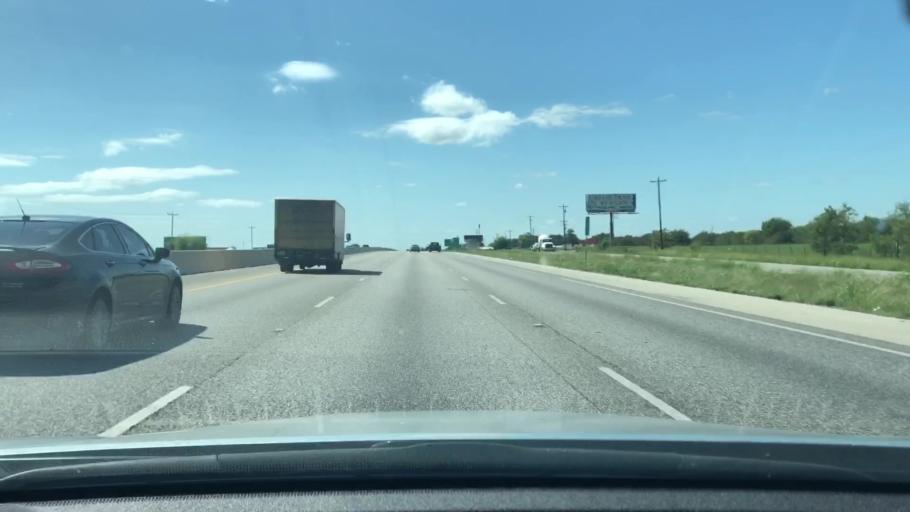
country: US
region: Texas
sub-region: Guadalupe County
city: Redwood
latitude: 29.8052
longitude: -98.0103
